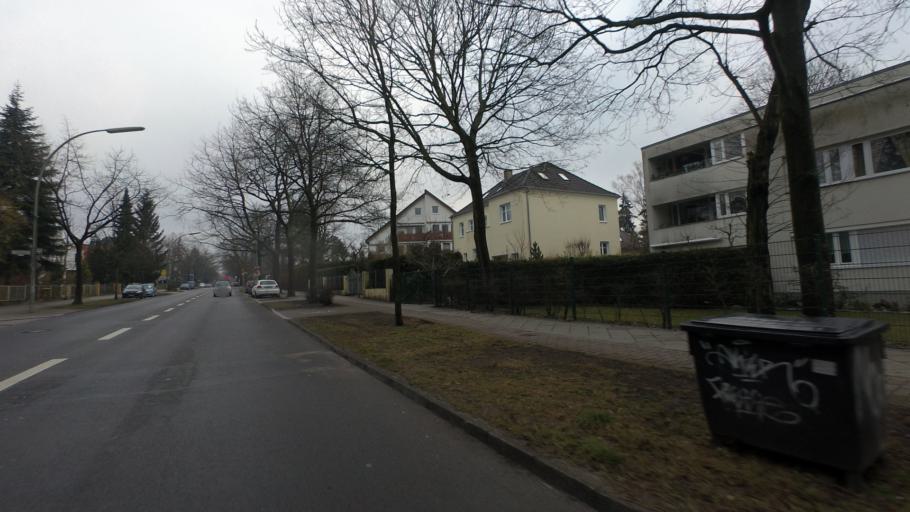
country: DE
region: Berlin
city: Hermsdorf
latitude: 52.6248
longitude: 13.3122
